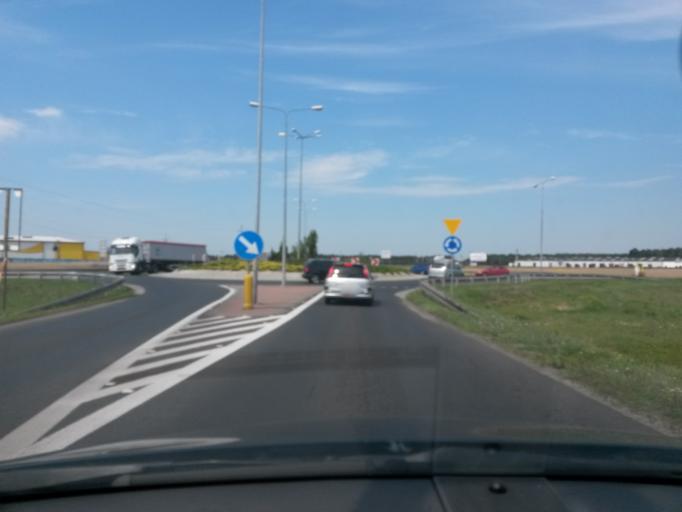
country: PL
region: Greater Poland Voivodeship
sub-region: Powiat sremski
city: Srem
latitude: 52.1060
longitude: 17.0434
